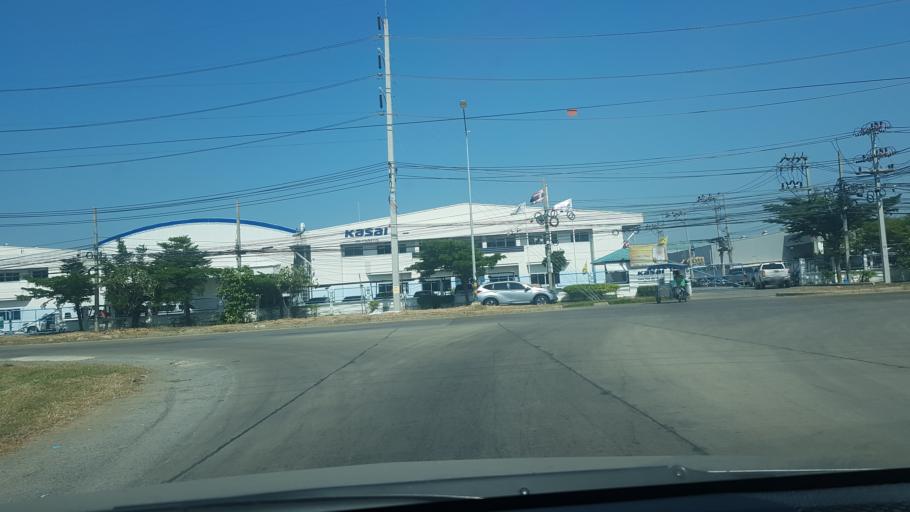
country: TH
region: Phra Nakhon Si Ayutthaya
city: Bang Pa-in
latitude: 14.2520
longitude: 100.6002
